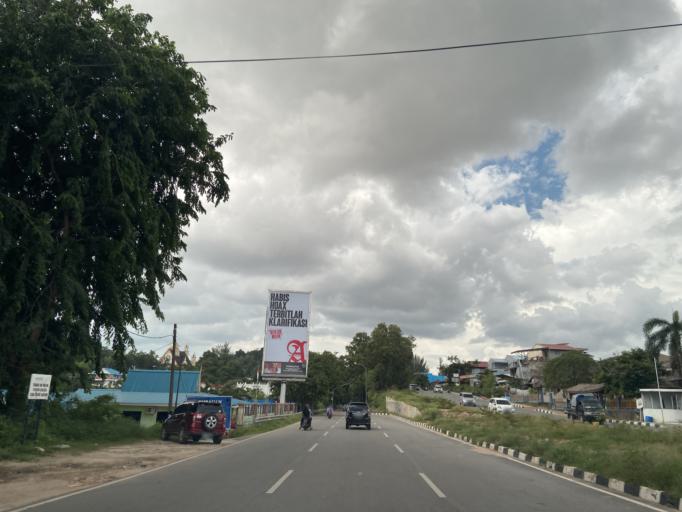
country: SG
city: Singapore
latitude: 1.1322
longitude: 104.0122
